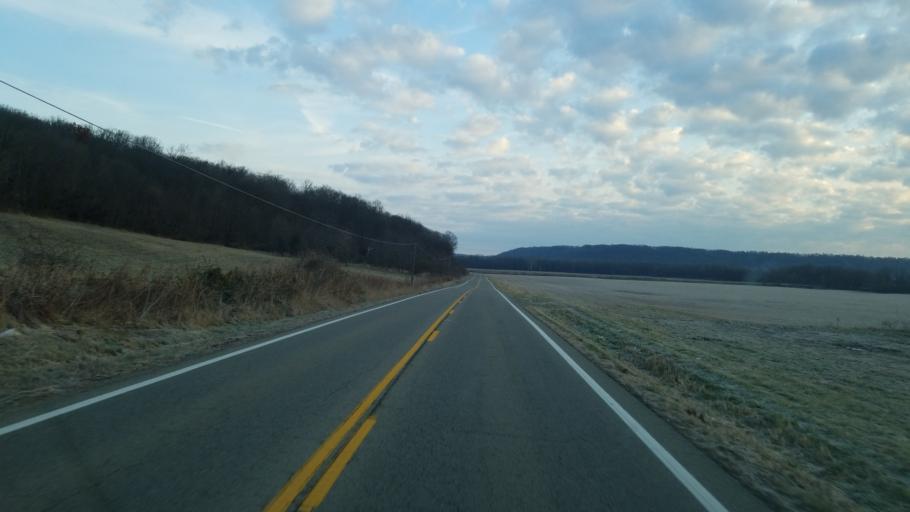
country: US
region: Ohio
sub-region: Ross County
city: Frankfort
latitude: 39.2617
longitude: -83.1786
